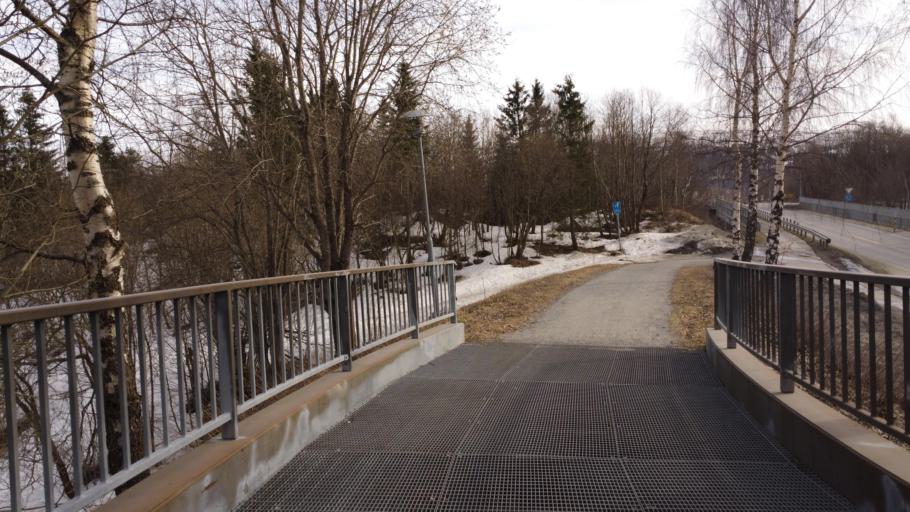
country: NO
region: Nordland
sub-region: Rana
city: Mo i Rana
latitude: 66.3264
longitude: 14.1593
